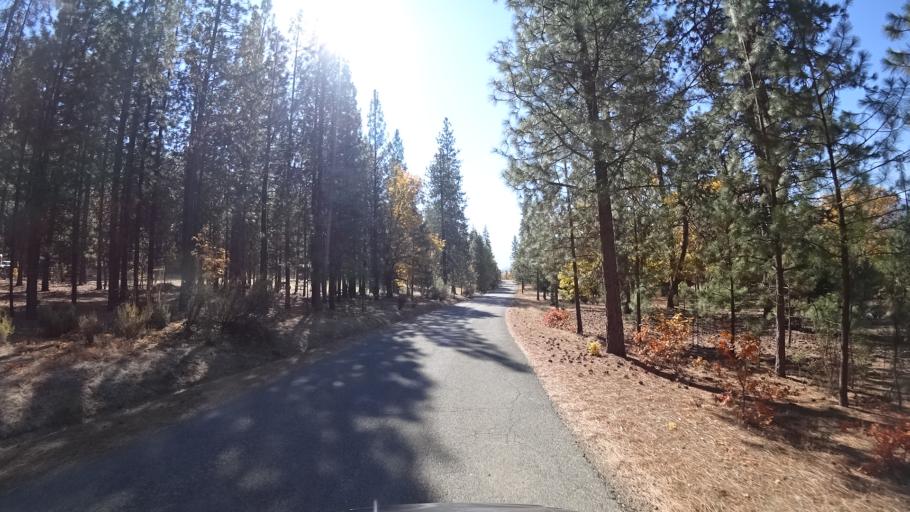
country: US
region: California
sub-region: Siskiyou County
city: Yreka
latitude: 41.6362
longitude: -122.8879
